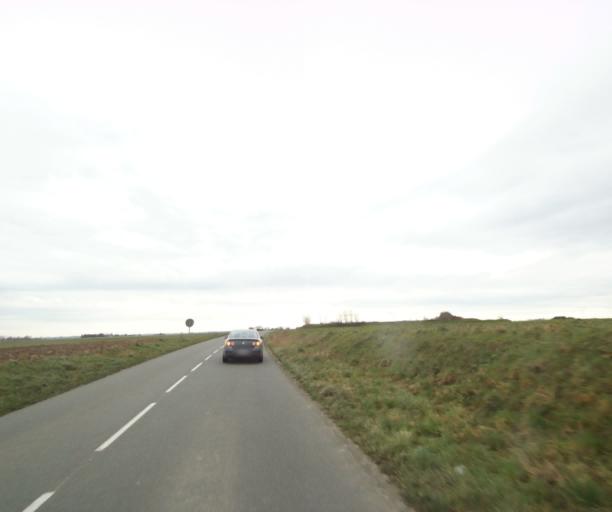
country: FR
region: Nord-Pas-de-Calais
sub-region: Departement du Nord
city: Curgies
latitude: 50.3541
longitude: 3.6146
